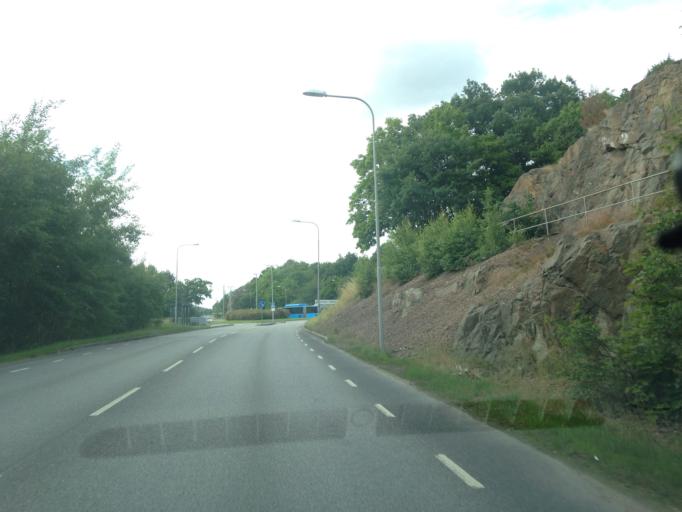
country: SE
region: Vaestra Goetaland
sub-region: Goteborg
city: Goeteborg
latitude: 57.7459
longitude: 11.9516
